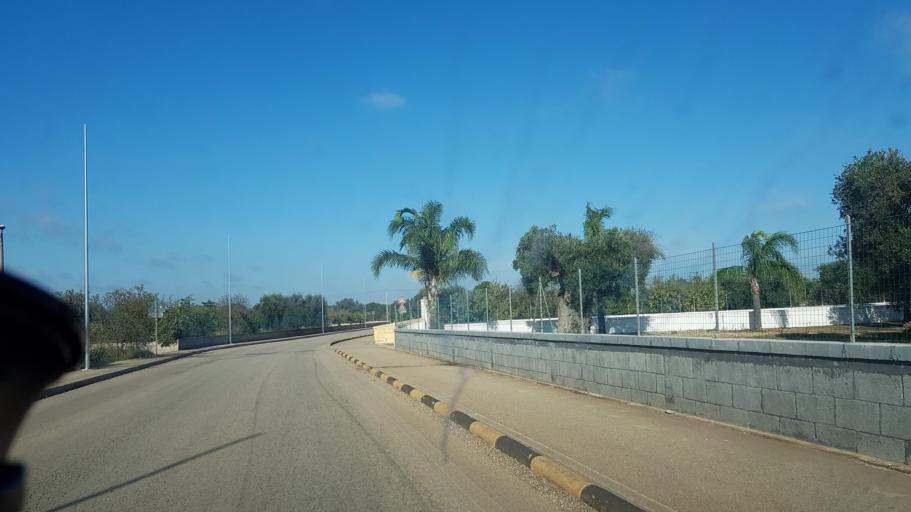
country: IT
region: Apulia
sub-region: Provincia di Brindisi
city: San Vito dei Normanni
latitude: 40.6594
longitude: 17.7168
